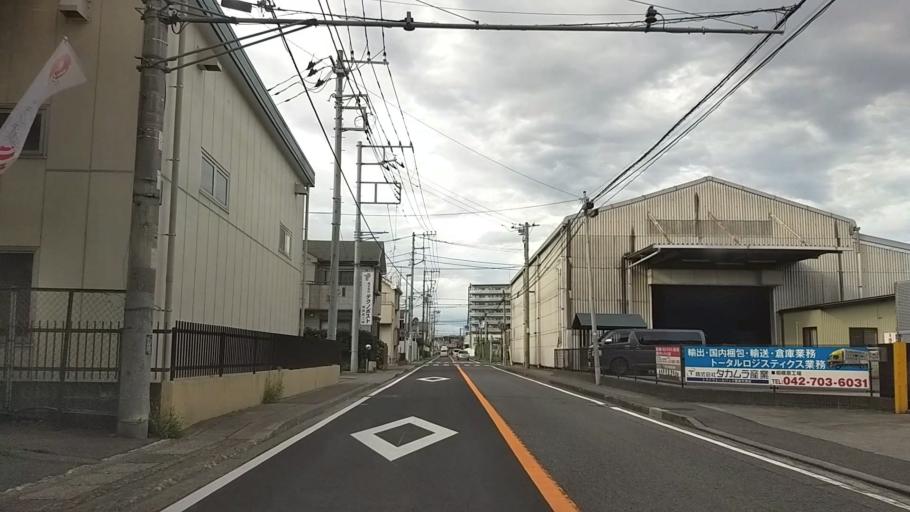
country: JP
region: Tokyo
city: Hachioji
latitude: 35.5798
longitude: 139.3418
